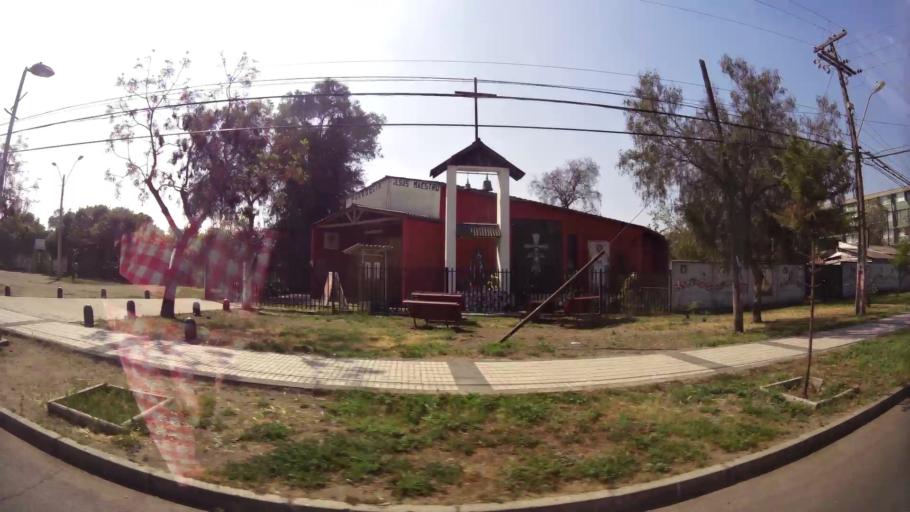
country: CL
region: Santiago Metropolitan
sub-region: Provincia de Santiago
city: Lo Prado
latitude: -33.4477
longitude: -70.6874
